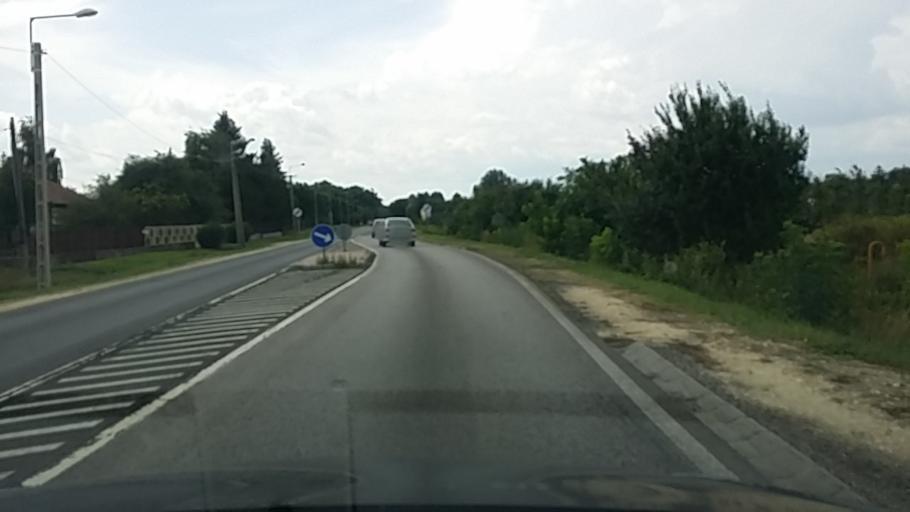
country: HU
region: Pest
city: Orkeny
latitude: 47.1212
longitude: 19.4388
